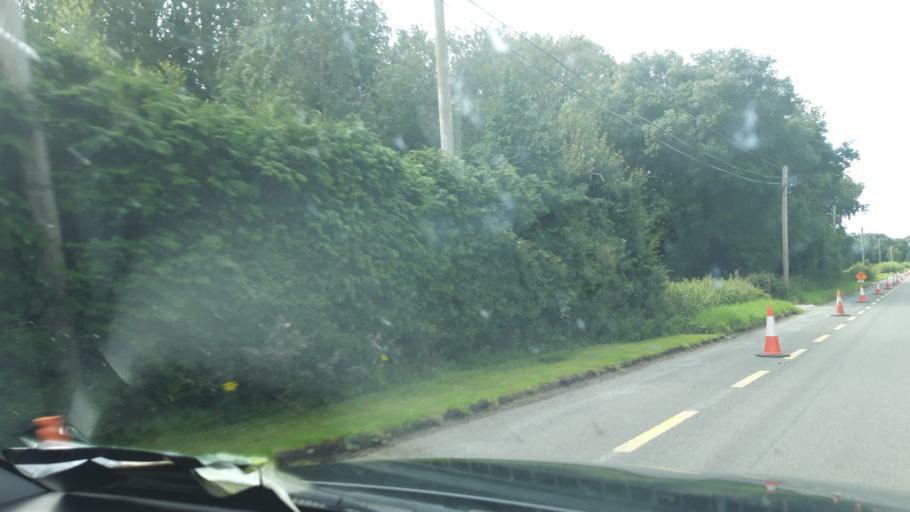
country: IE
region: Leinster
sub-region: Kilkenny
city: Callan
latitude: 52.5594
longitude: -7.3679
